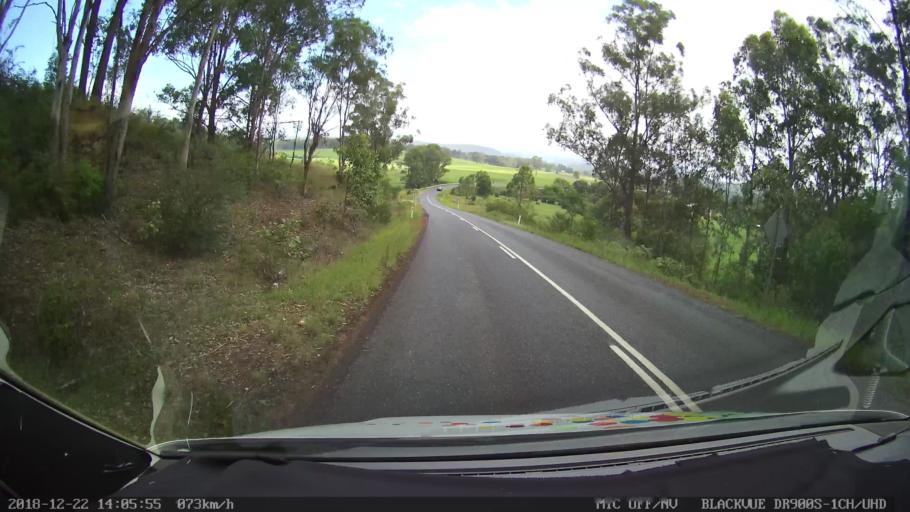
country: AU
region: New South Wales
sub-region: Clarence Valley
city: Coutts Crossing
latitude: -29.9500
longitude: 152.7285
